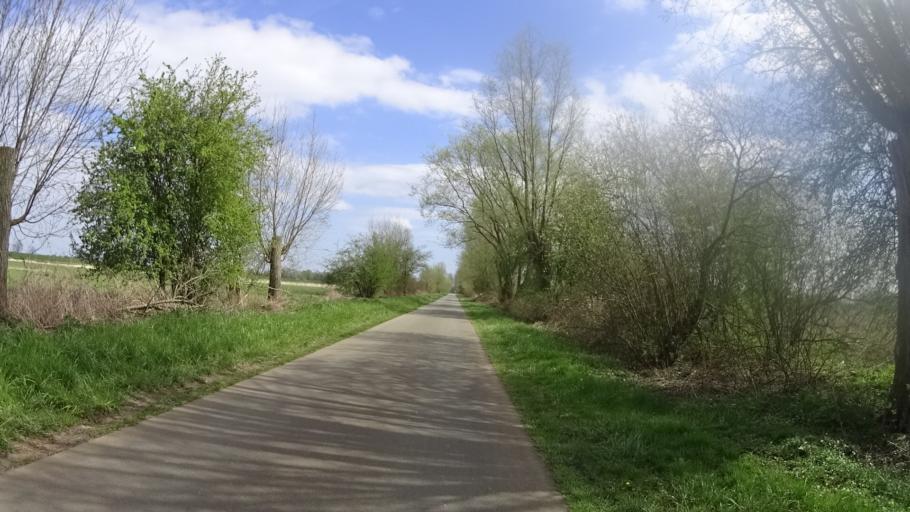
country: DE
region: Lower Saxony
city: Rhede
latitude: 53.0552
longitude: 7.3051
